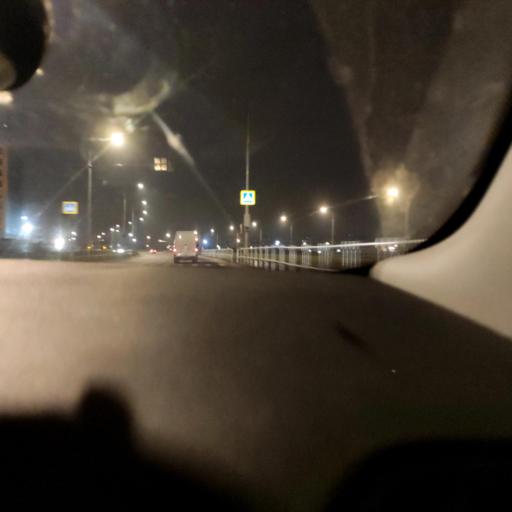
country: RU
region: Moscow
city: Nekrasovka
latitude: 55.7124
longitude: 37.9327
